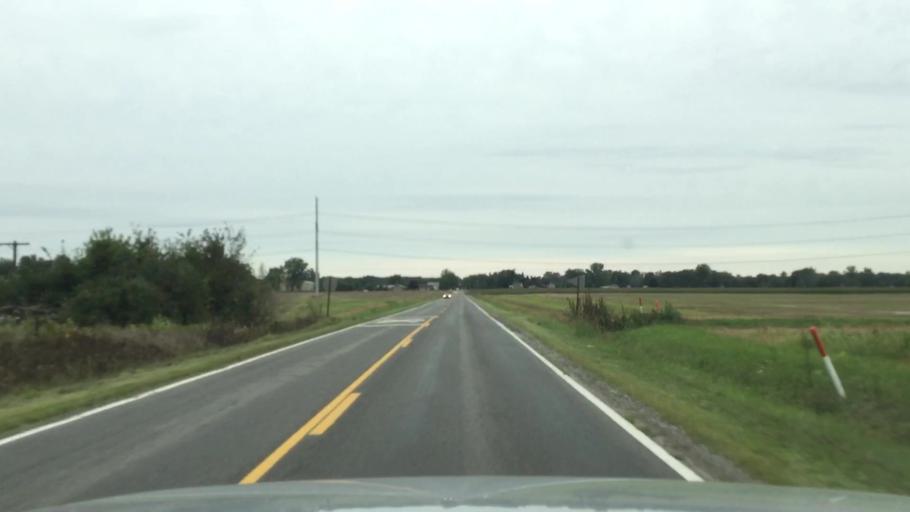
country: US
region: Michigan
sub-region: Washtenaw County
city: Milan
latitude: 42.1166
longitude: -83.6961
